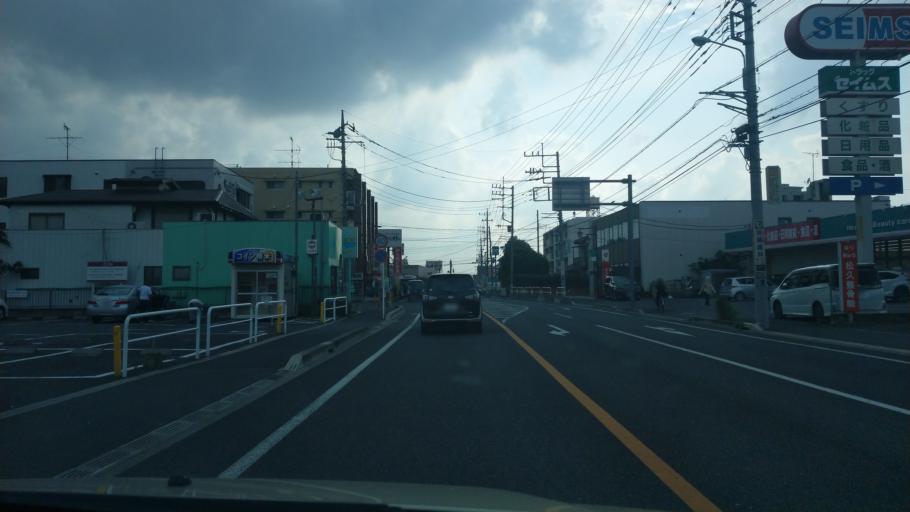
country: JP
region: Saitama
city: Saitama
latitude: 35.8798
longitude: 139.6721
